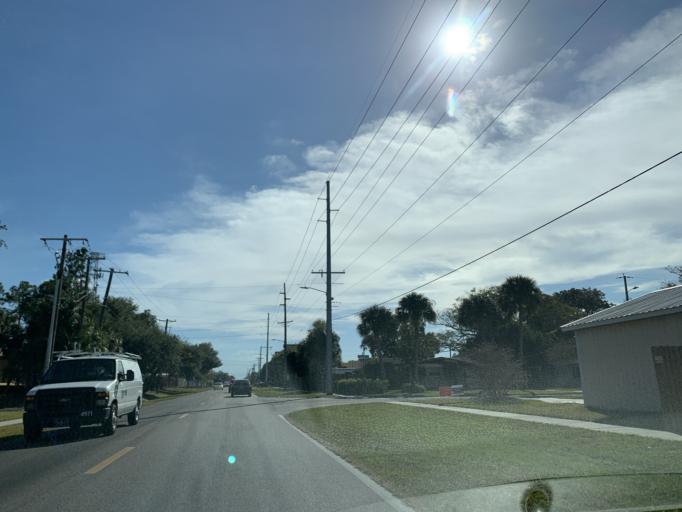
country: US
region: Florida
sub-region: Hillsborough County
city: Tampa
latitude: 27.8890
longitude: -82.5184
